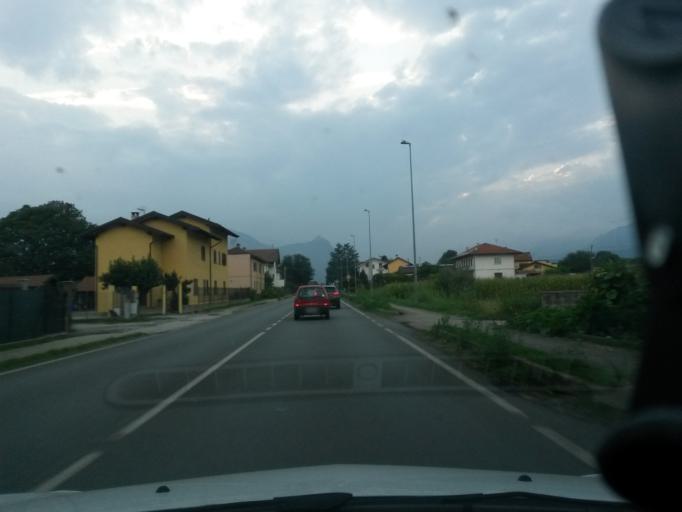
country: IT
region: Piedmont
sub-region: Provincia di Torino
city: Drubiaglio-Grangia
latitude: 45.0948
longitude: 7.4225
